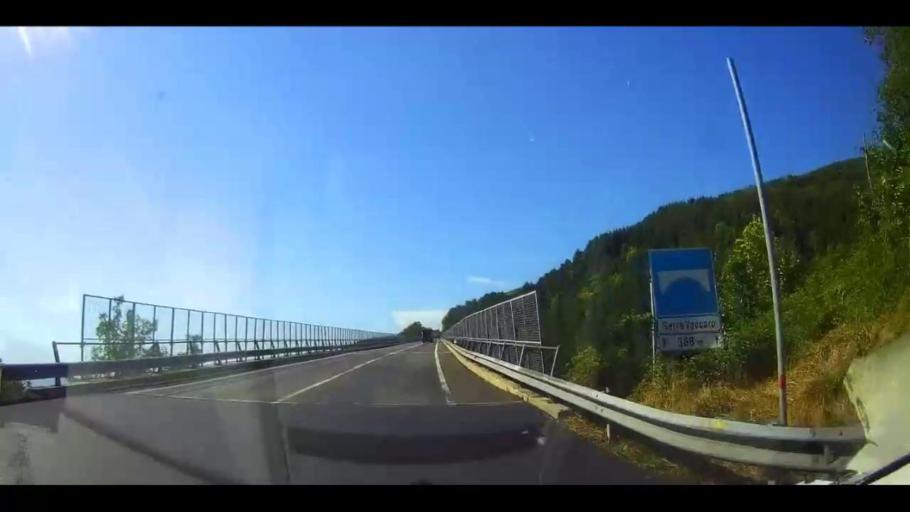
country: IT
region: Calabria
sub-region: Provincia di Cosenza
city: Celico
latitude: 39.3214
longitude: 16.3692
